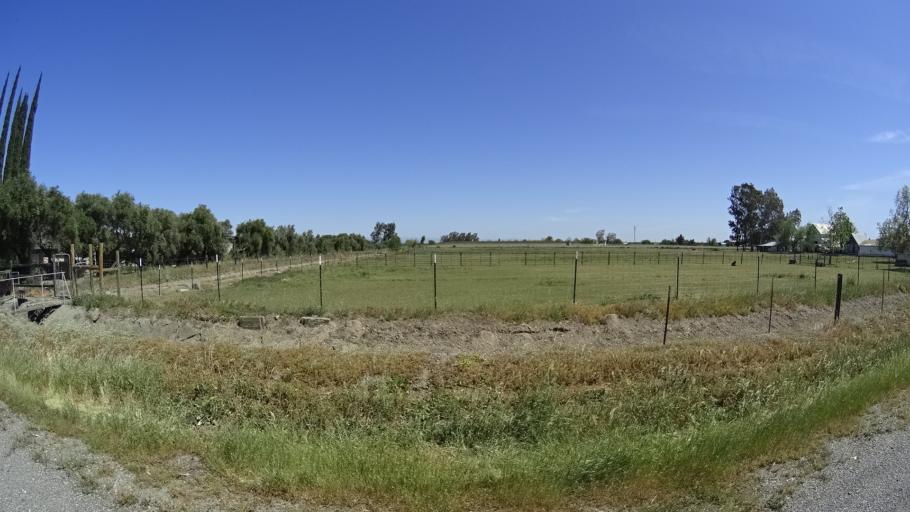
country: US
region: California
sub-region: Glenn County
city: Orland
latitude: 39.7359
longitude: -122.1596
